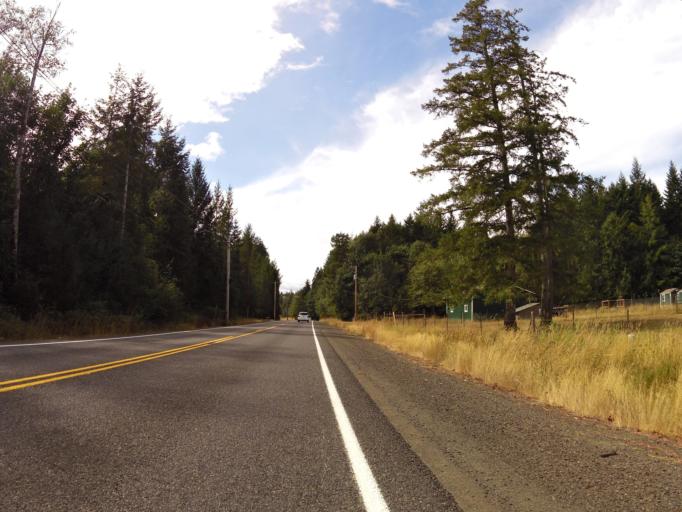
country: US
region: Washington
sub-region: Mason County
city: Shelton
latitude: 47.1568
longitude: -123.0500
